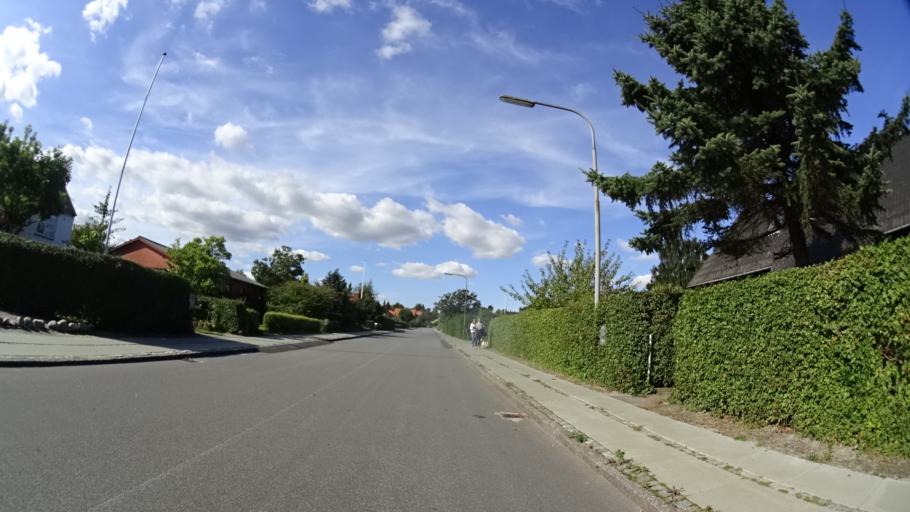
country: DK
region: Central Jutland
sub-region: Arhus Kommune
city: Arhus
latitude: 56.1609
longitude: 10.1671
